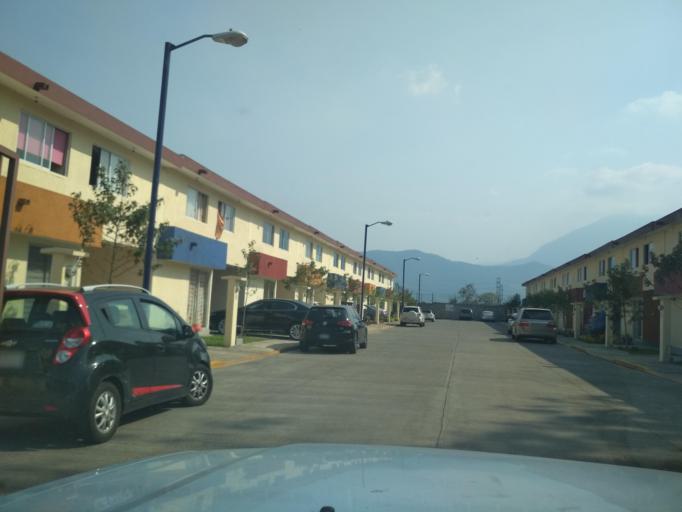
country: MX
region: Veracruz
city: Jalapilla
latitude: 18.8387
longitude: -97.0844
